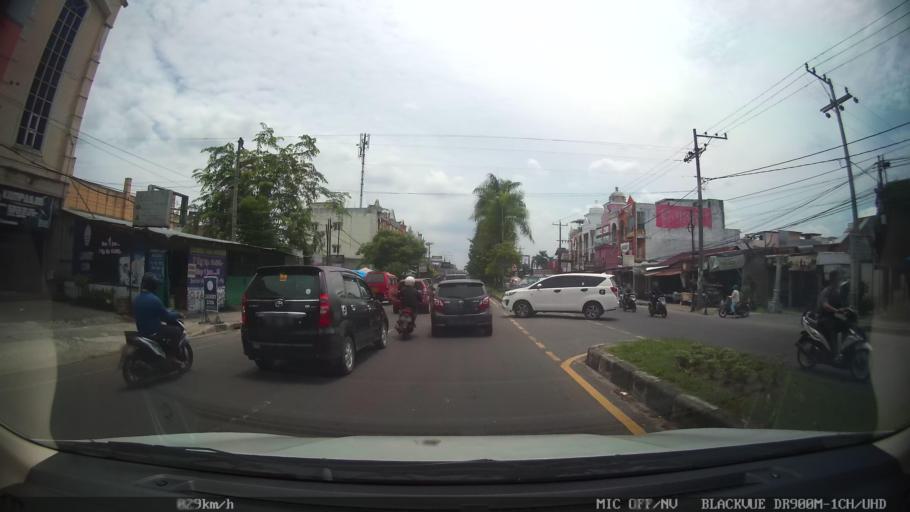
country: ID
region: North Sumatra
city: Deli Tua
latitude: 3.5292
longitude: 98.6377
